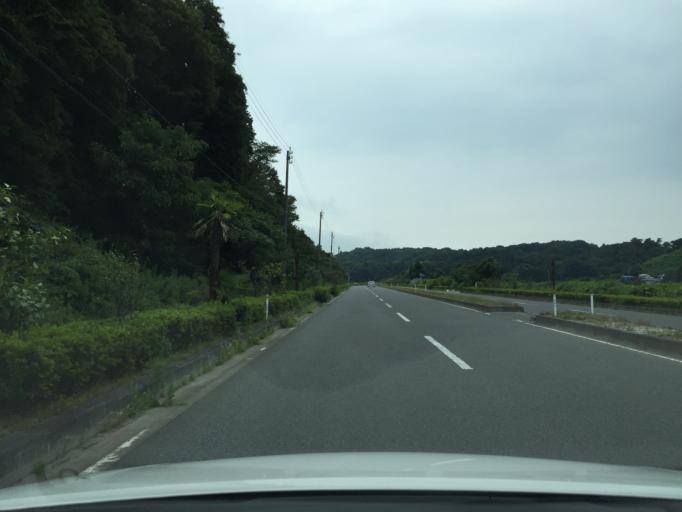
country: JP
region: Fukushima
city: Iwaki
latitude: 36.9601
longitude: 140.9195
